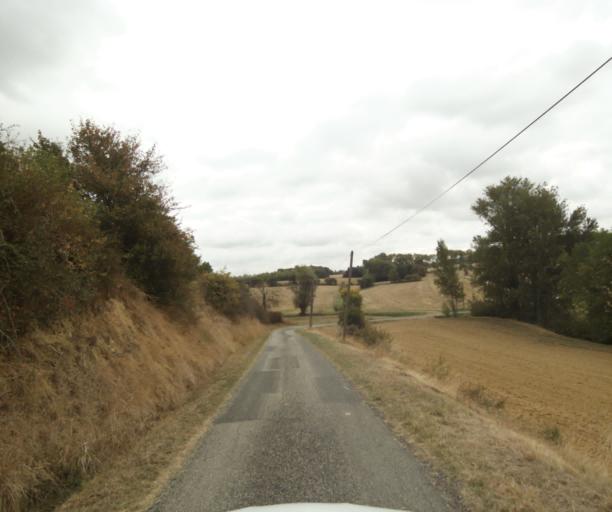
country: FR
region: Midi-Pyrenees
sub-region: Departement de la Haute-Garonne
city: Villefranche-de-Lauragais
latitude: 43.4173
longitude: 1.7359
